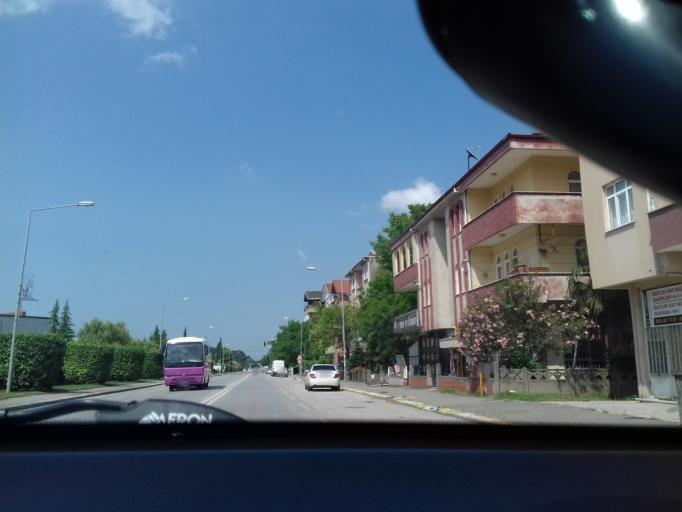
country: TR
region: Sakarya
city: Adapazari
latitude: 40.7240
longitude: 30.3721
